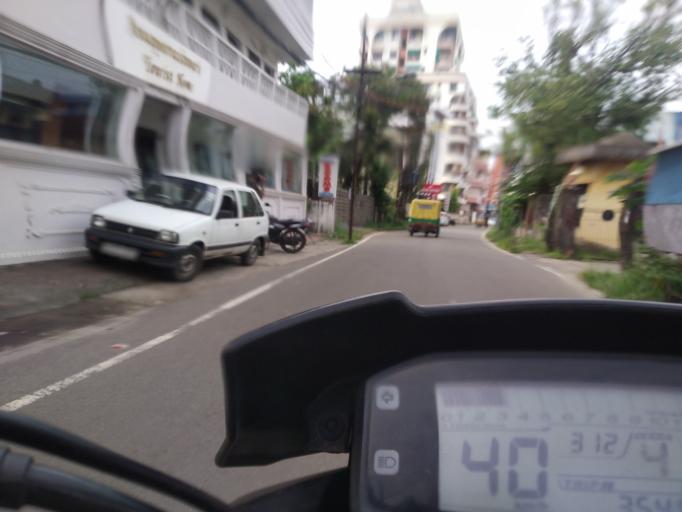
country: IN
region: Kerala
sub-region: Ernakulam
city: Cochin
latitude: 9.9692
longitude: 76.2890
